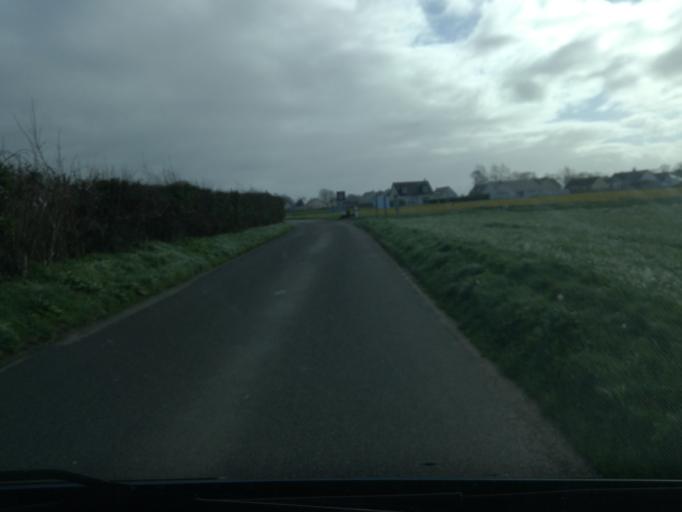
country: FR
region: Haute-Normandie
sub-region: Departement de la Seine-Maritime
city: Yport
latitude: 49.7378
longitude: 0.3298
